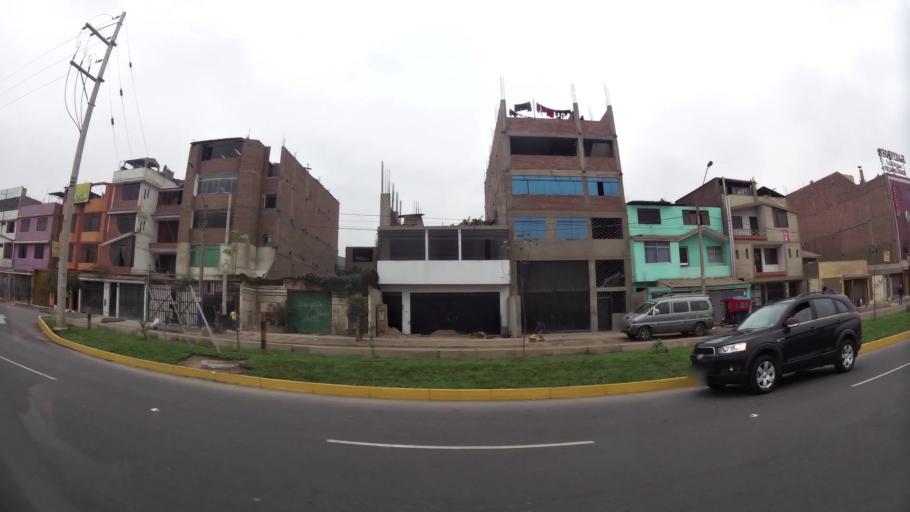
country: PE
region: Lima
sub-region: Lima
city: Vitarte
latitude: -12.0437
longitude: -76.9316
